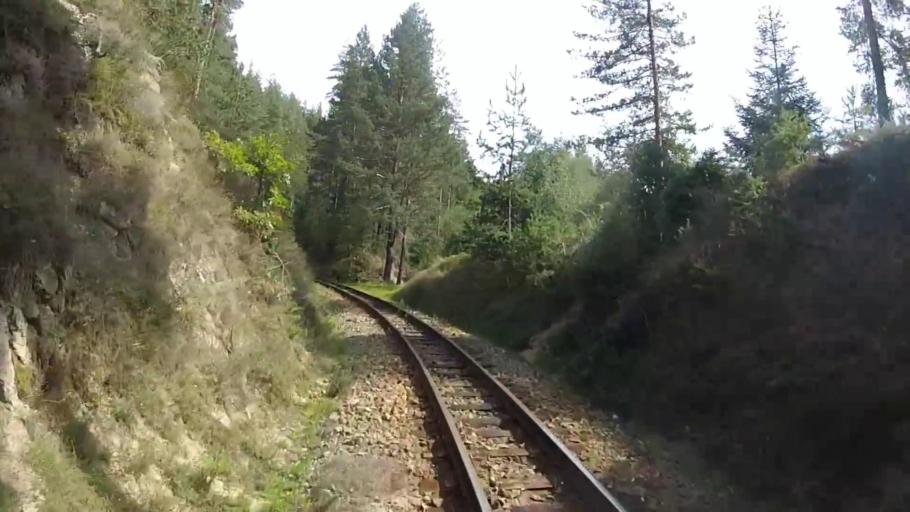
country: BG
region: Blagoevgrad
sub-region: Obshtina Yakoruda
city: Yakoruda
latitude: 42.0313
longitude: 23.7577
